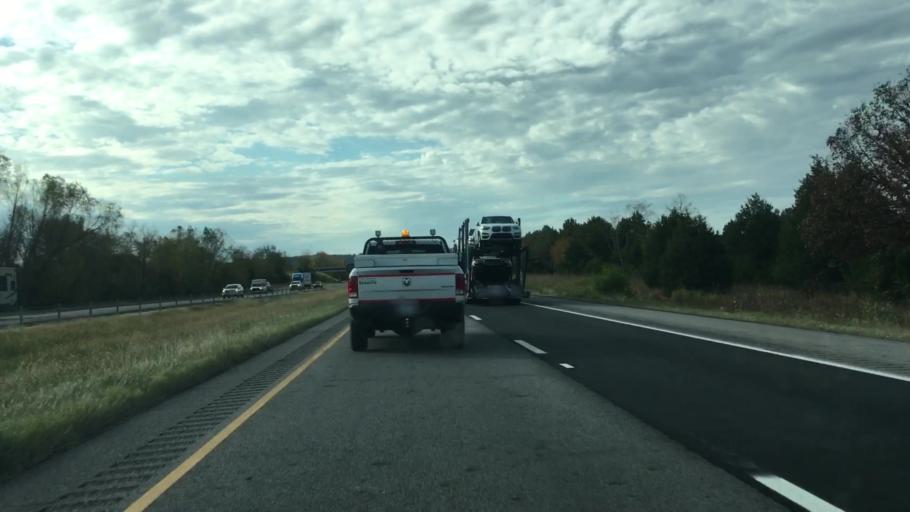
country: US
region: Arkansas
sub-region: Pope County
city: Atkins
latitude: 35.2503
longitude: -92.8853
